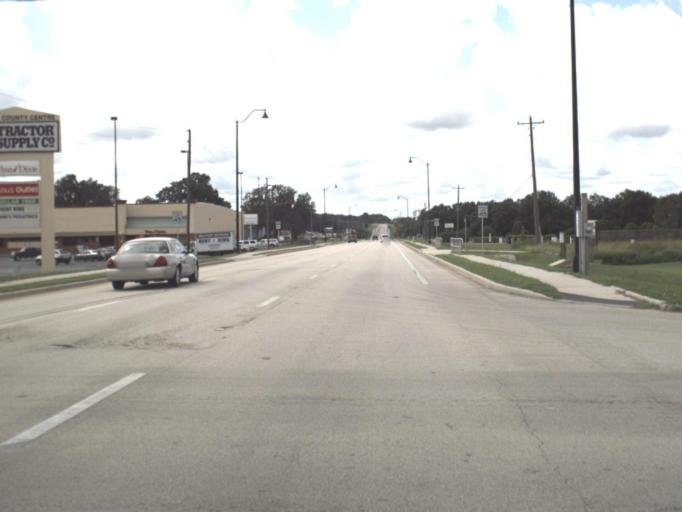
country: US
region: Florida
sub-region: Hardee County
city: Wauchula
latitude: 27.5330
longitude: -81.8094
